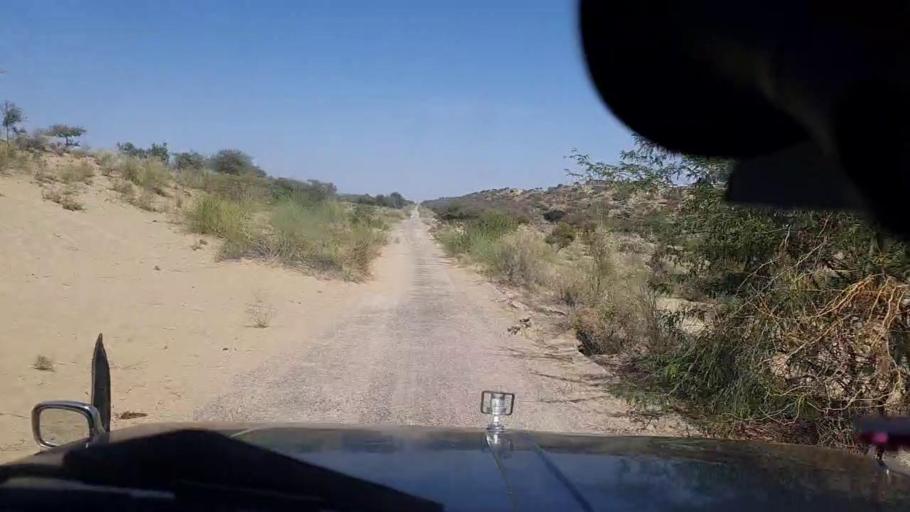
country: PK
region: Sindh
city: Diplo
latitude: 24.4107
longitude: 69.6455
